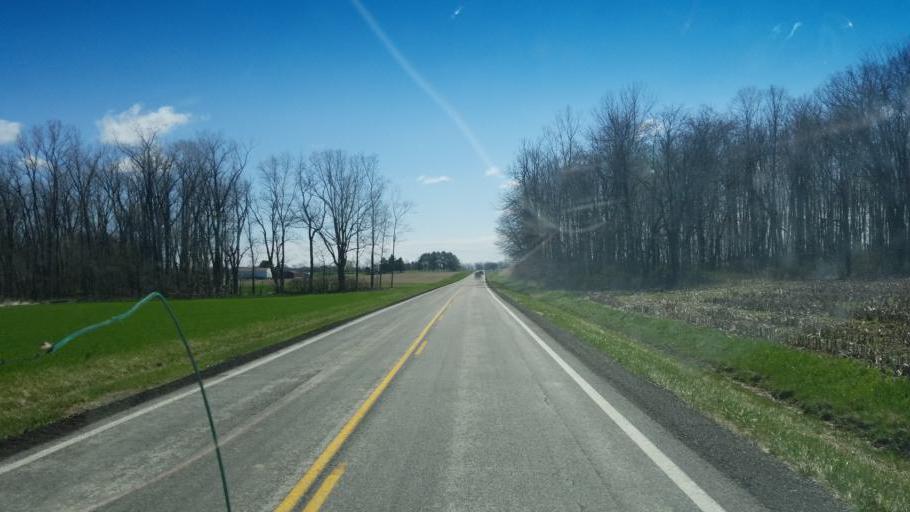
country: US
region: Ohio
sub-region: Crawford County
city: Crestline
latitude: 40.8578
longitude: -82.8007
